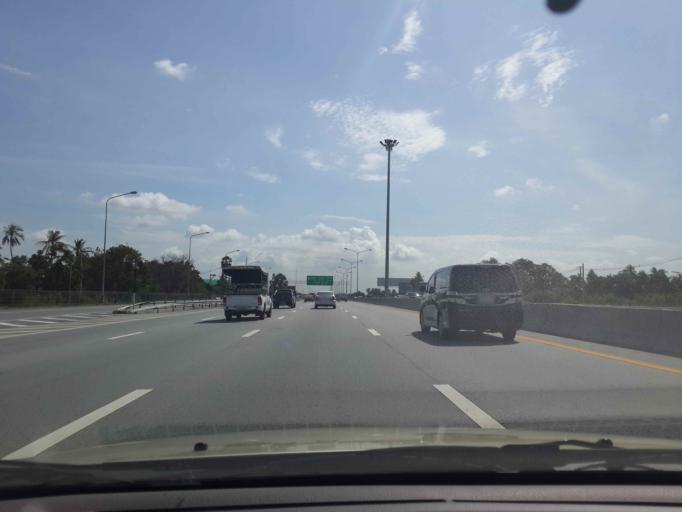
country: TH
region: Chon Buri
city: Chon Buri
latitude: 13.3171
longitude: 101.0093
